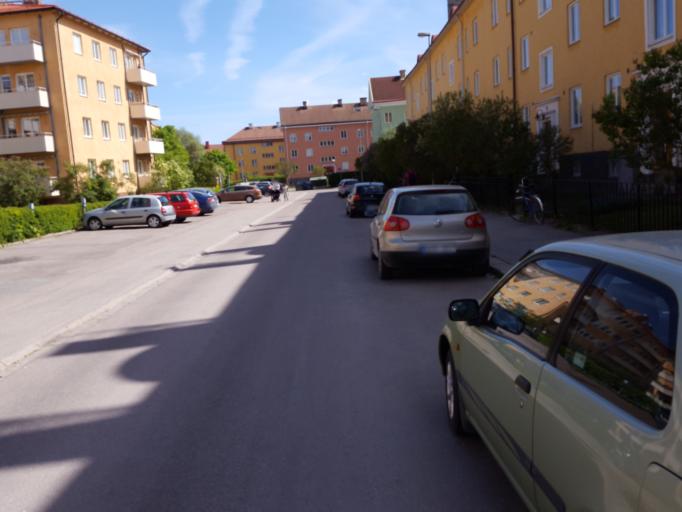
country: SE
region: Uppsala
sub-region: Uppsala Kommun
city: Uppsala
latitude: 59.8599
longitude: 17.6535
